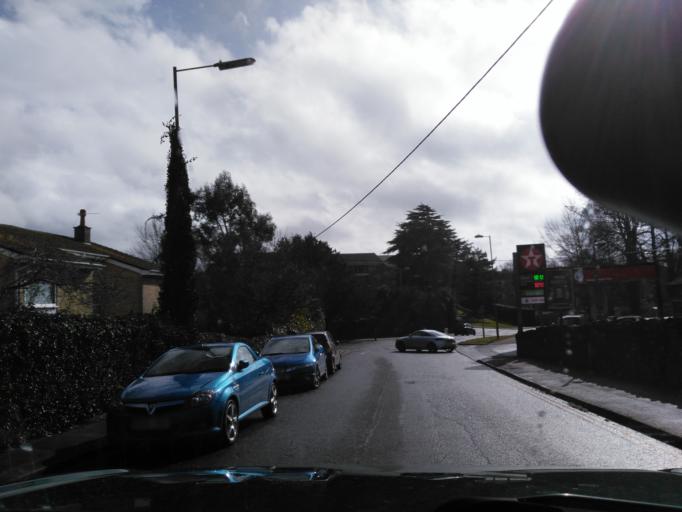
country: GB
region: England
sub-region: Wiltshire
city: Bradford-on-Avon
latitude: 51.3495
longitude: -2.2431
